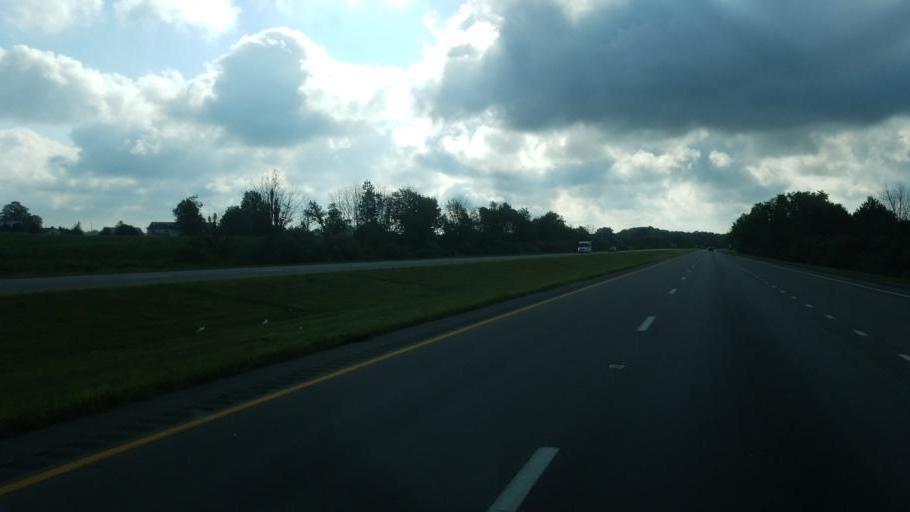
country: US
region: Ohio
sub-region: Wayne County
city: Dalton
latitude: 40.7897
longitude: -81.6271
